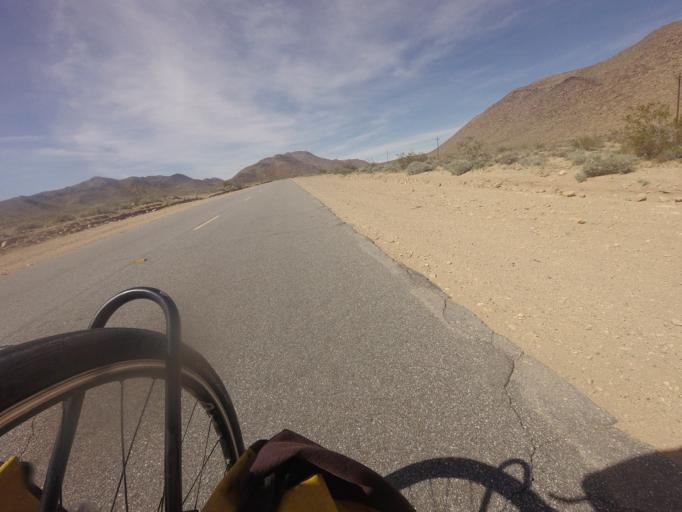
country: US
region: California
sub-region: San Bernardino County
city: Searles Valley
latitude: 35.5771
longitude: -117.4548
